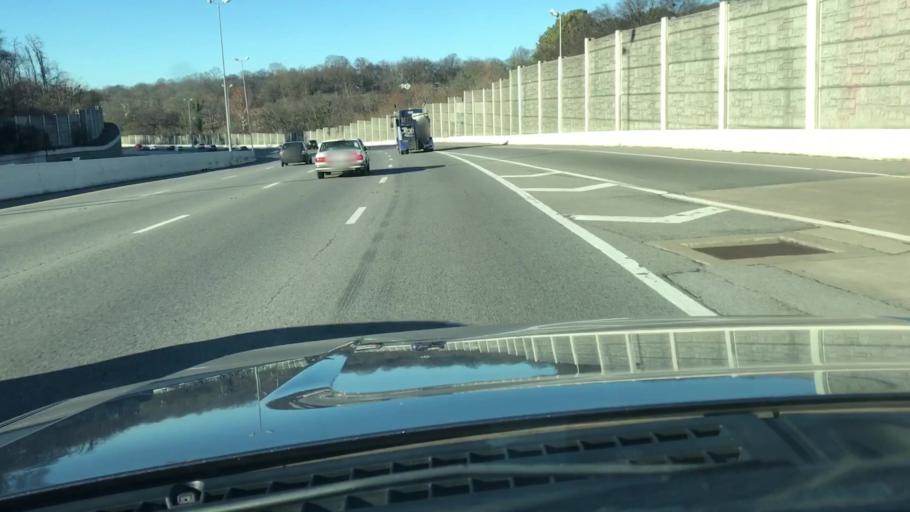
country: US
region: Tennessee
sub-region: Davidson County
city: Lakewood
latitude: 36.1719
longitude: -86.6887
